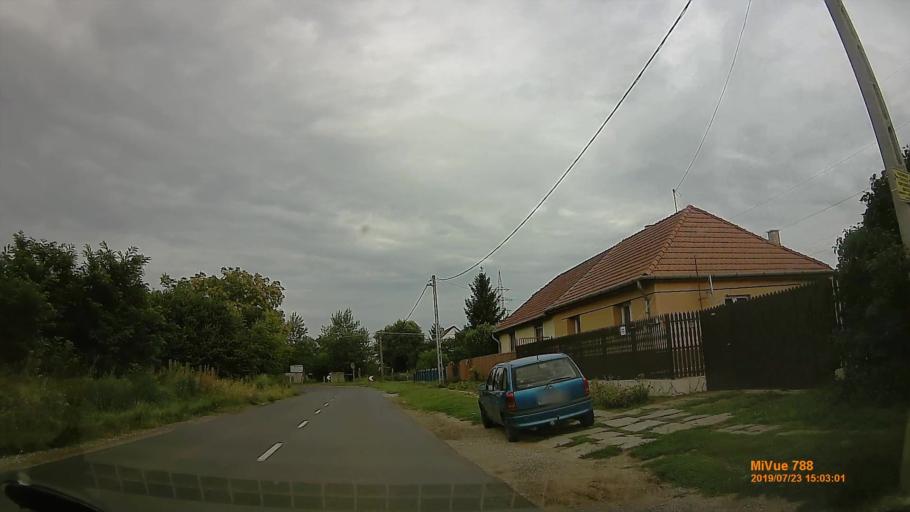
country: HU
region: Szabolcs-Szatmar-Bereg
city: Nyiregyhaza
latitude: 47.9319
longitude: 21.7072
